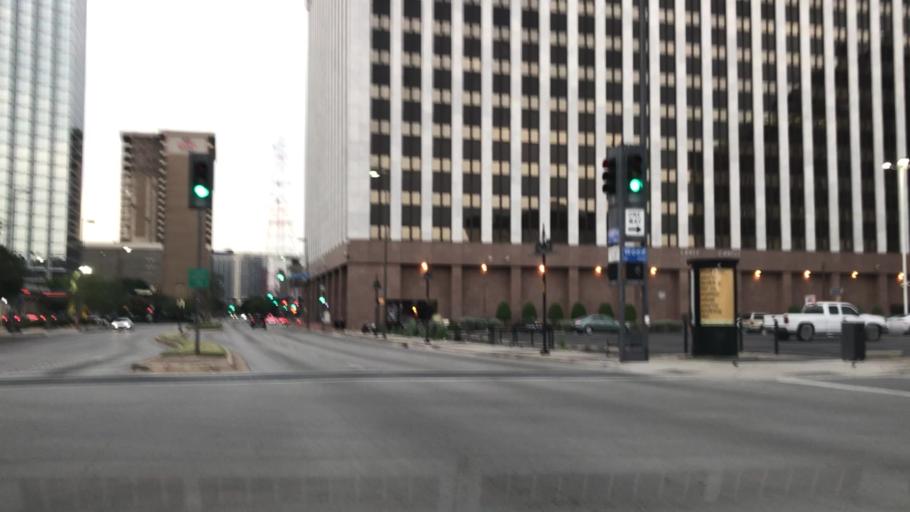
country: US
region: Texas
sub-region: Dallas County
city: Dallas
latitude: 32.7776
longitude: -96.8024
